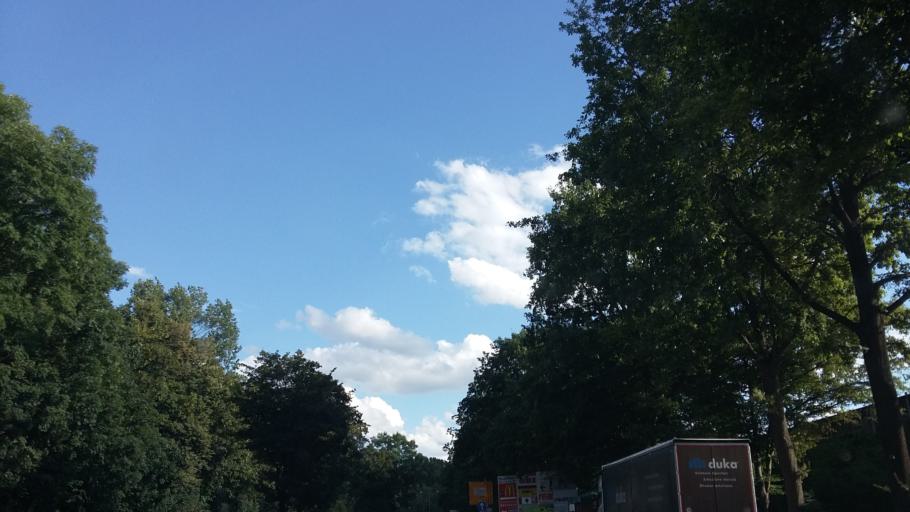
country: DE
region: Bavaria
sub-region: Swabia
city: Augsburg
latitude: 48.4013
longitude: 10.9205
